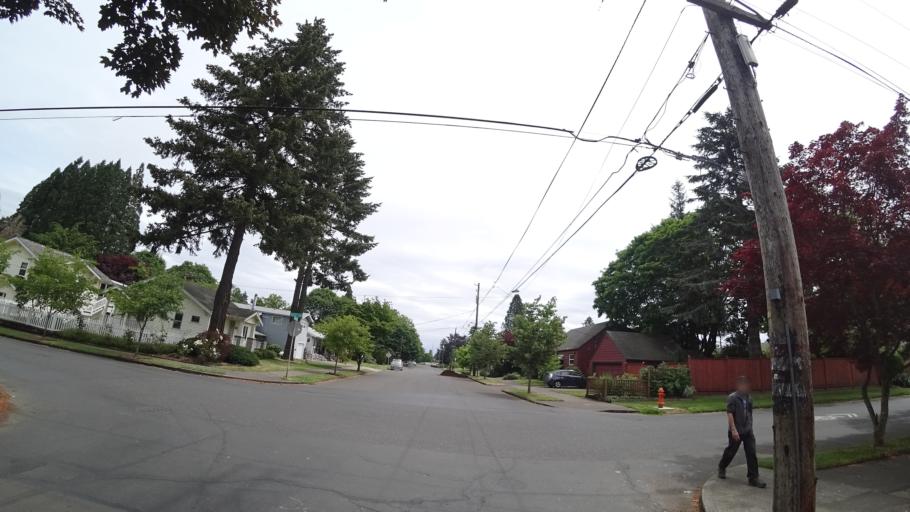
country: US
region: Oregon
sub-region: Multnomah County
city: Portland
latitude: 45.5651
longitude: -122.6257
